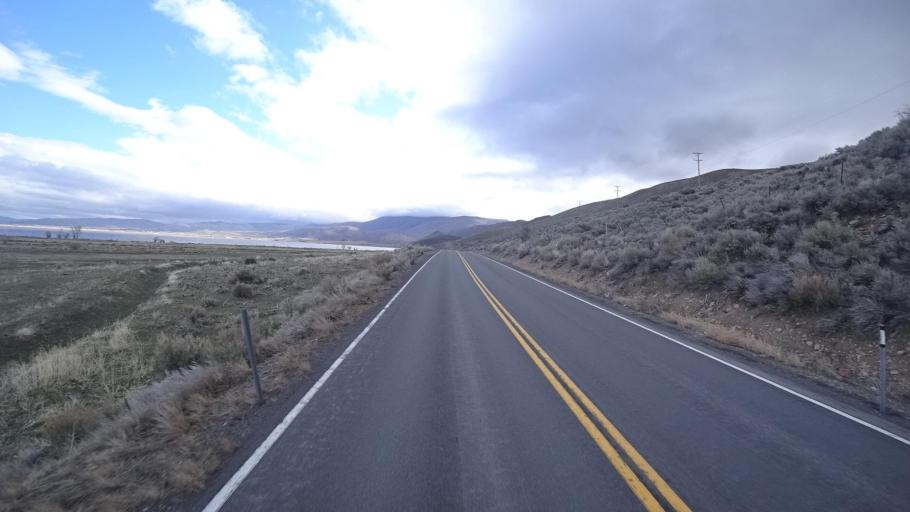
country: US
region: Nevada
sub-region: Carson City
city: Carson City
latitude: 39.2272
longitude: -119.7910
